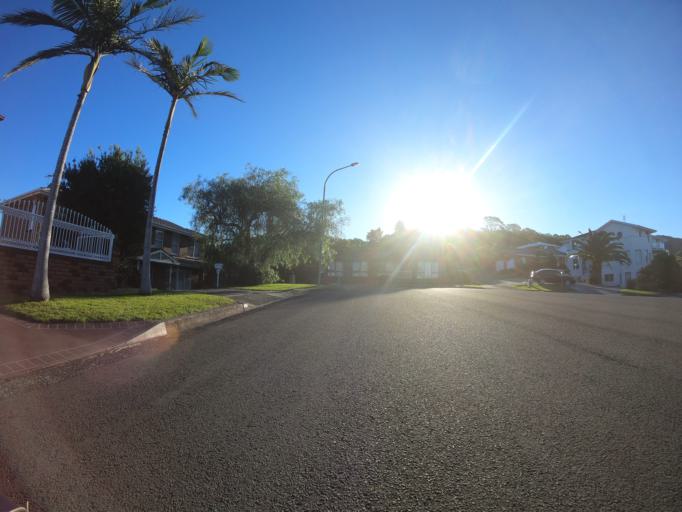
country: AU
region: New South Wales
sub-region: Wollongong
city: Mount Keira
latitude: -34.4213
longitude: 150.8500
